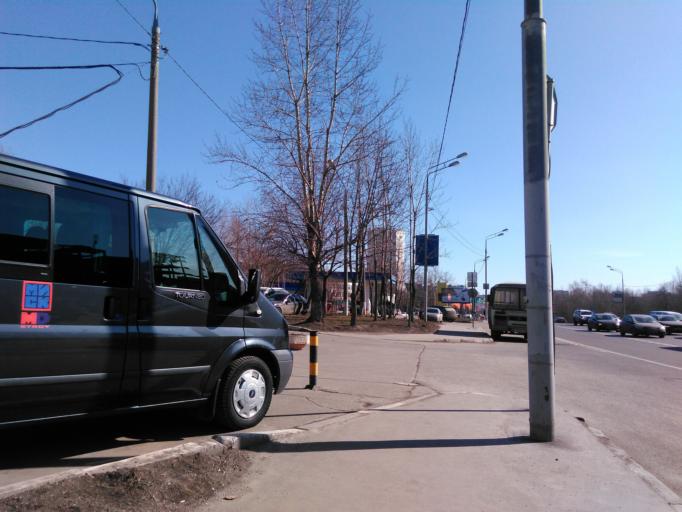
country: RU
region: Moskovskaya
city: Cheremushki
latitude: 55.6570
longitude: 37.5300
